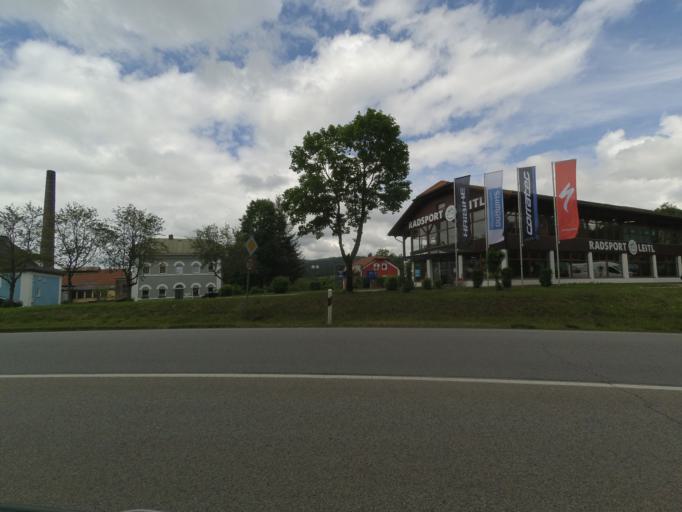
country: DE
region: Bavaria
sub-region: Lower Bavaria
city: Zwiesel
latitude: 49.0318
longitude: 13.2336
